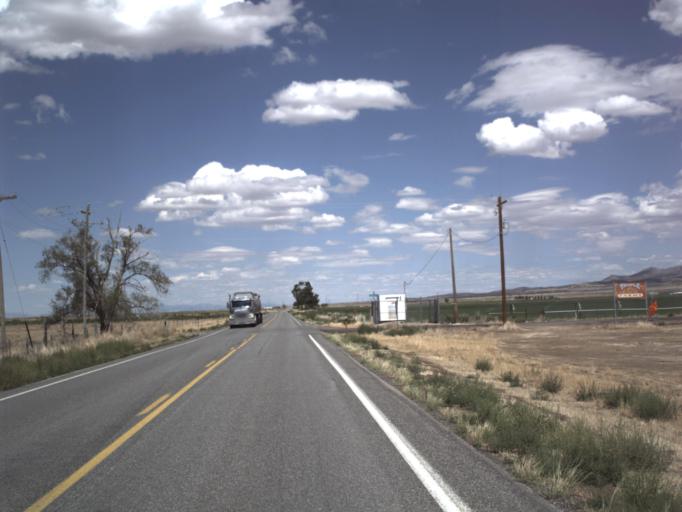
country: US
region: Utah
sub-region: Millard County
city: Delta
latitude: 39.1968
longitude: -112.4100
